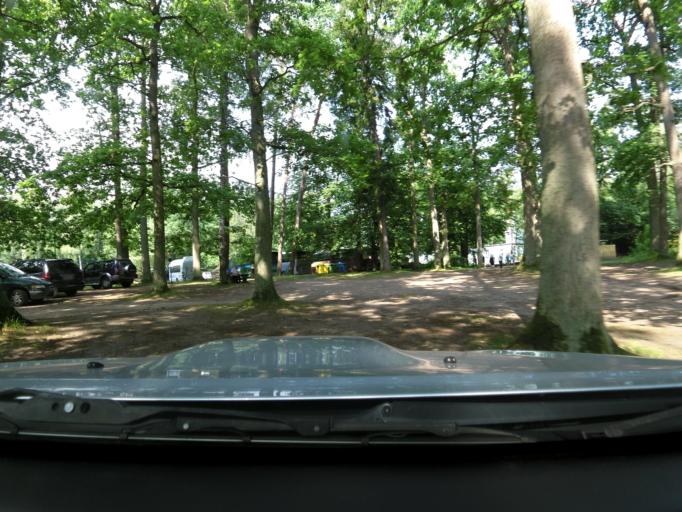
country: PL
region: Warmian-Masurian Voivodeship
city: Gierloz
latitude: 54.0796
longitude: 21.4949
